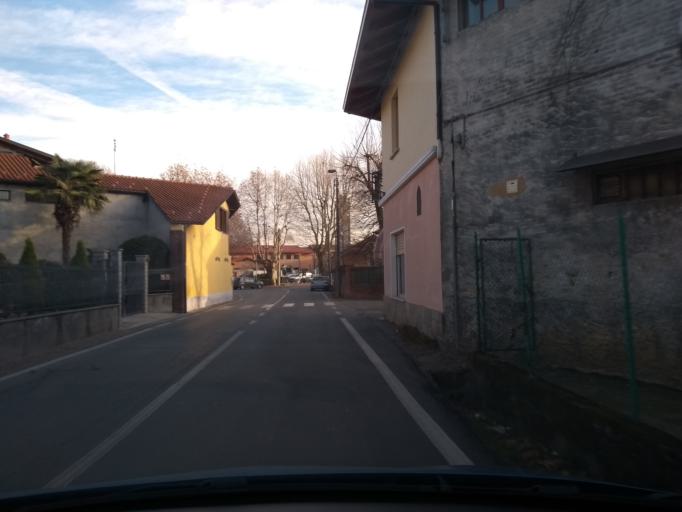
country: IT
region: Piedmont
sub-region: Provincia di Torino
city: Balangero
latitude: 45.2730
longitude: 7.5196
